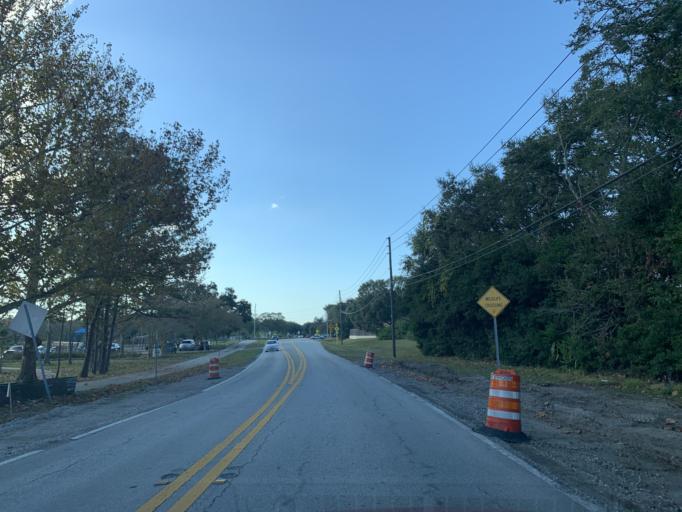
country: US
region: Florida
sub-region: Pinellas County
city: Safety Harbor
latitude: 27.9789
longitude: -82.7391
